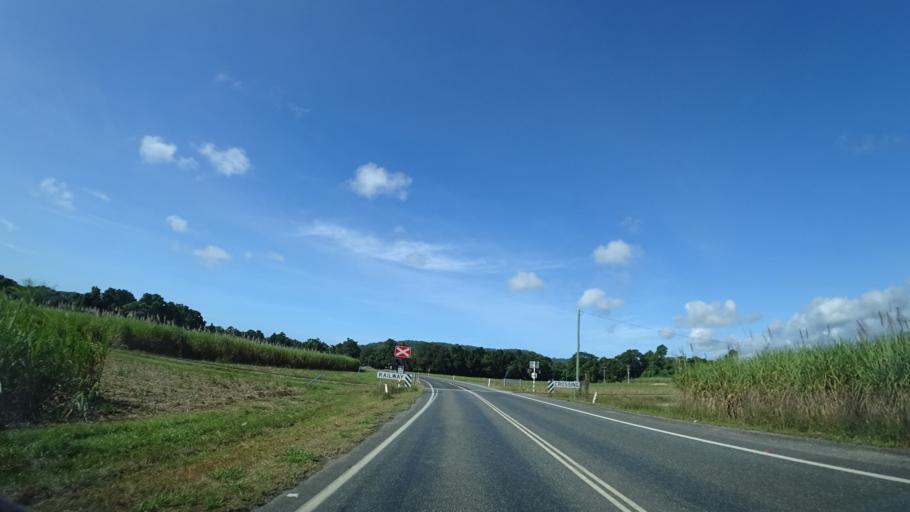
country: AU
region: Queensland
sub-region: Cairns
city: Port Douglas
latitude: -16.4852
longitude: 145.3804
